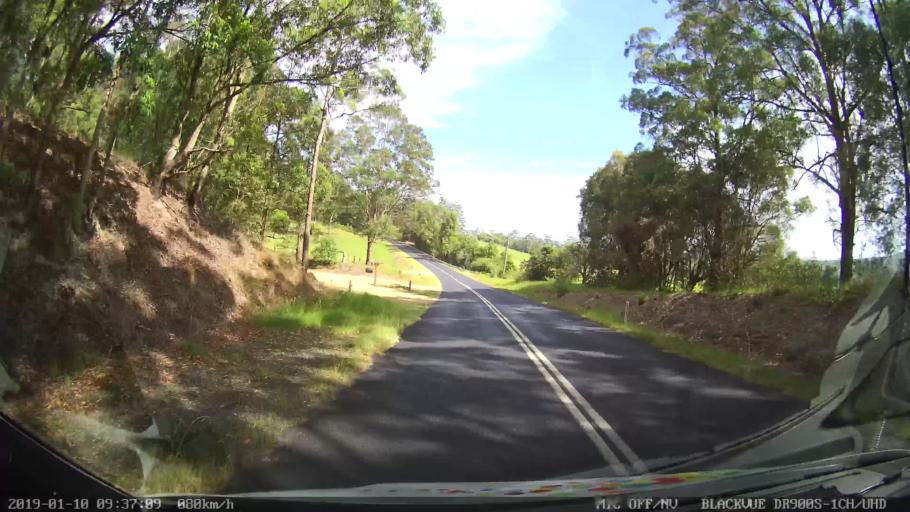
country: AU
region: New South Wales
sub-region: Coffs Harbour
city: Nana Glen
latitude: -30.1907
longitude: 153.0118
